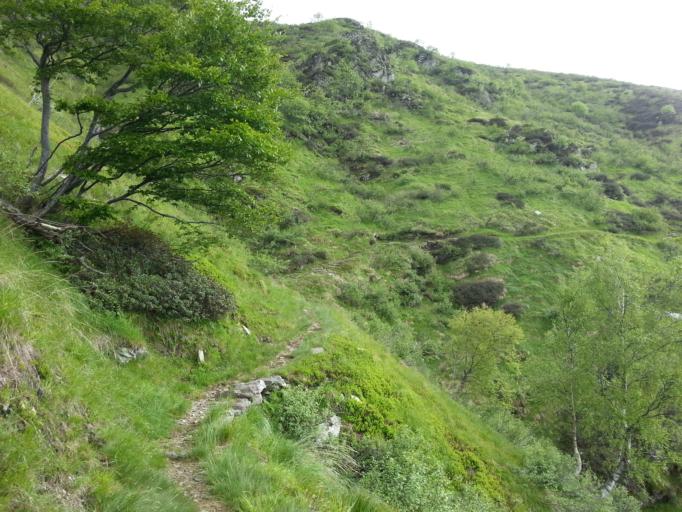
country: CH
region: Ticino
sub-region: Locarno District
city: Magadino
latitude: 46.0936
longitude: 8.8572
